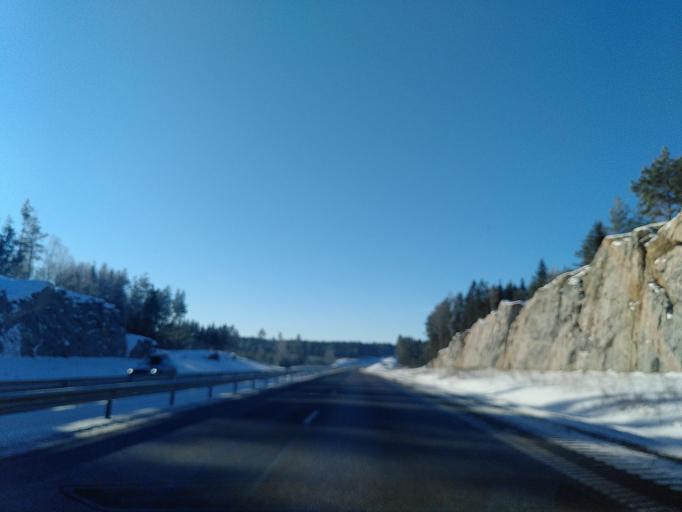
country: SE
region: Vaestra Goetaland
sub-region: Vargarda Kommun
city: Jonstorp
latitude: 57.9854
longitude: 12.7186
